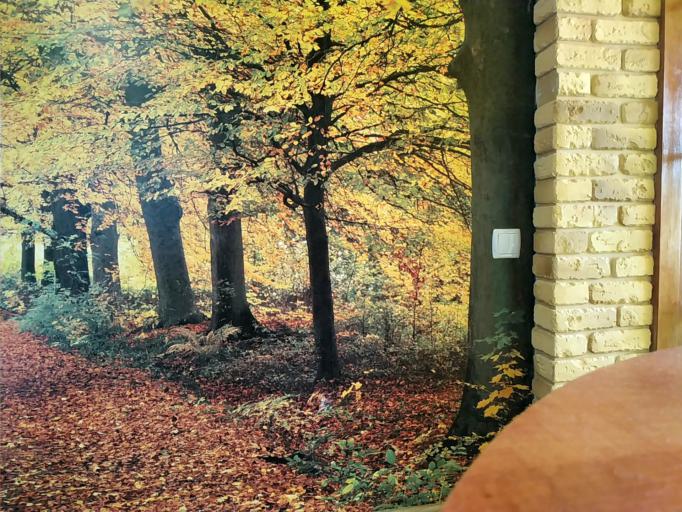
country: RU
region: Pskov
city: Dno
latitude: 57.9101
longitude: 30.1837
